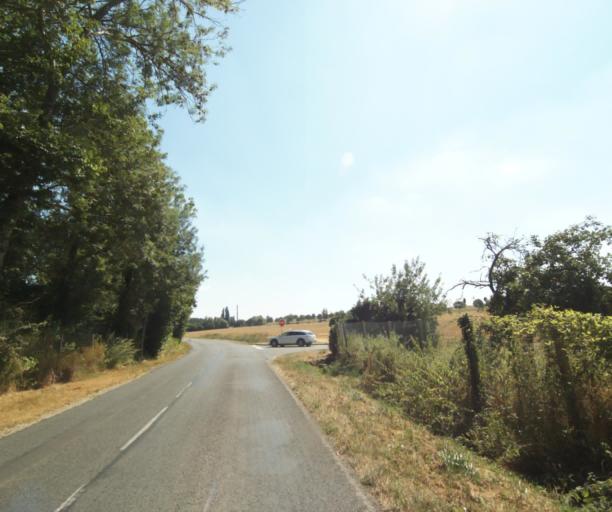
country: FR
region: Ile-de-France
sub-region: Departement de Seine-et-Marne
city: Chanteloup-en-Brie
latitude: 48.8539
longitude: 2.7304
